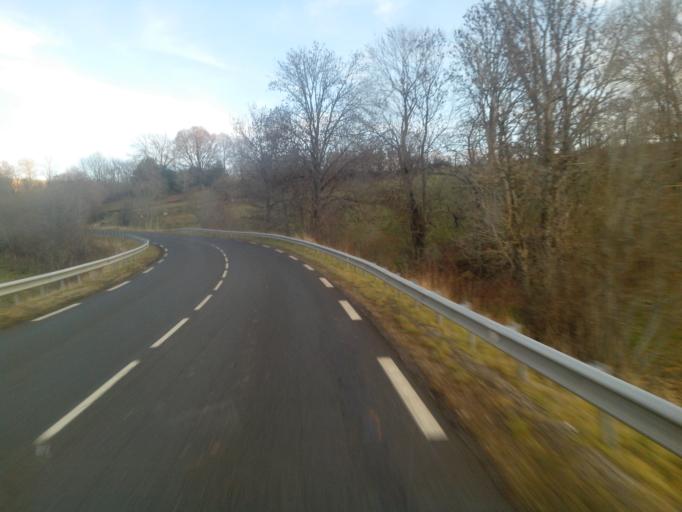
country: FR
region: Auvergne
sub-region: Departement du Cantal
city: Riom-es-Montagnes
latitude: 45.2351
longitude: 2.7284
